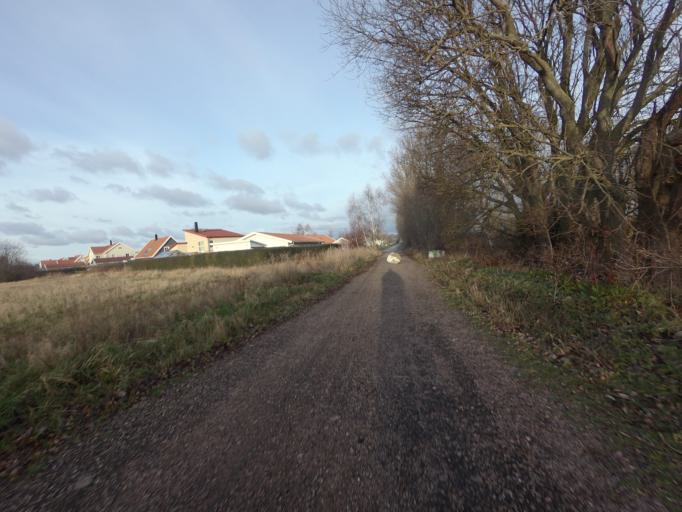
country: SE
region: Skane
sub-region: Hoganas Kommun
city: Hoganas
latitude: 56.1787
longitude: 12.5775
